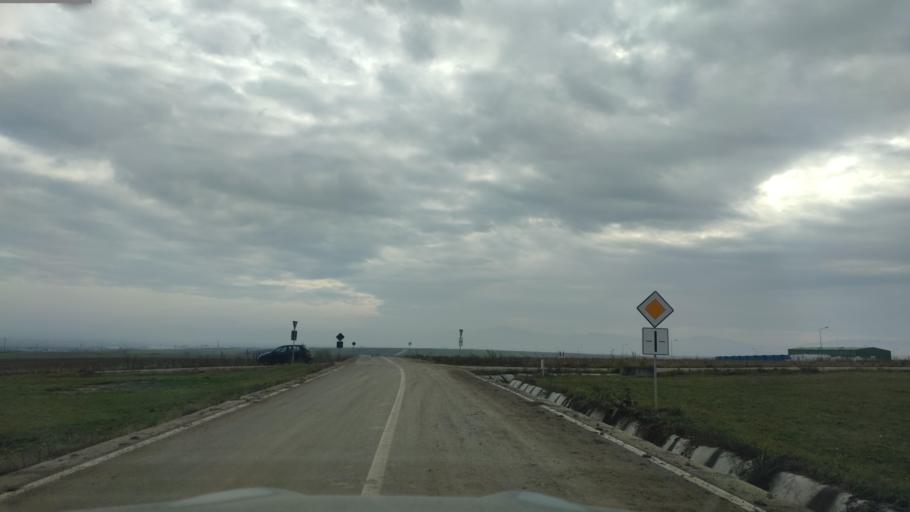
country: RO
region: Harghita
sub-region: Comuna Subcetate
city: Subcetate
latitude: 46.8300
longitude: 25.4431
